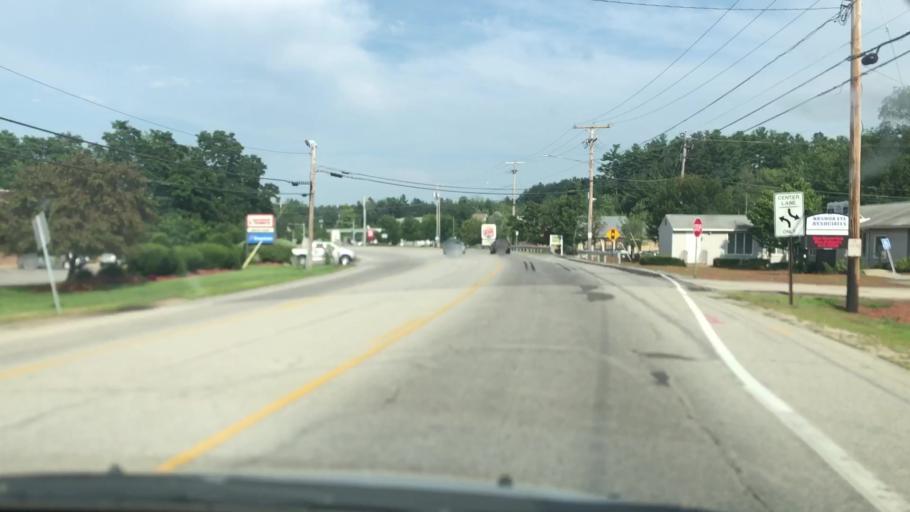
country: US
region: New Hampshire
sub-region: Hillsborough County
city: Milford
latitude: 42.8237
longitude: -71.6269
